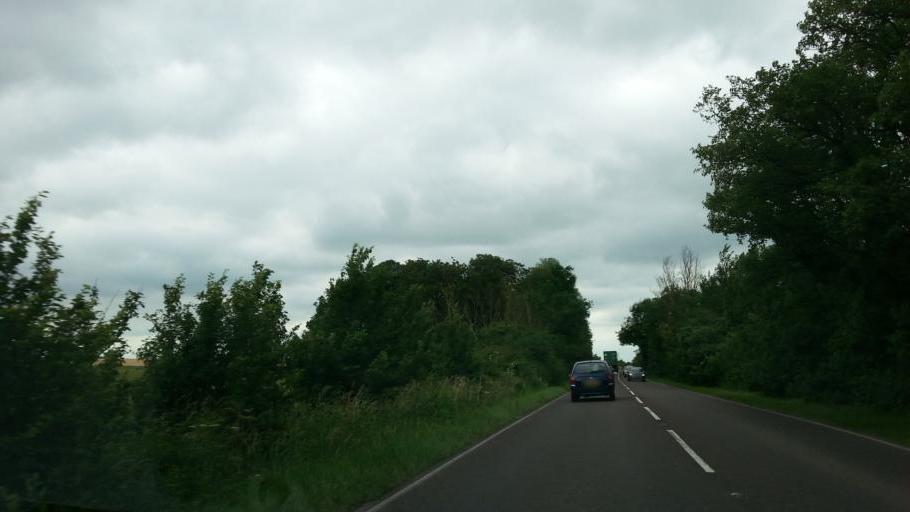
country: GB
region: England
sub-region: Cambridgeshire
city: Papworth Everard
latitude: 52.2602
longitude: -0.1260
